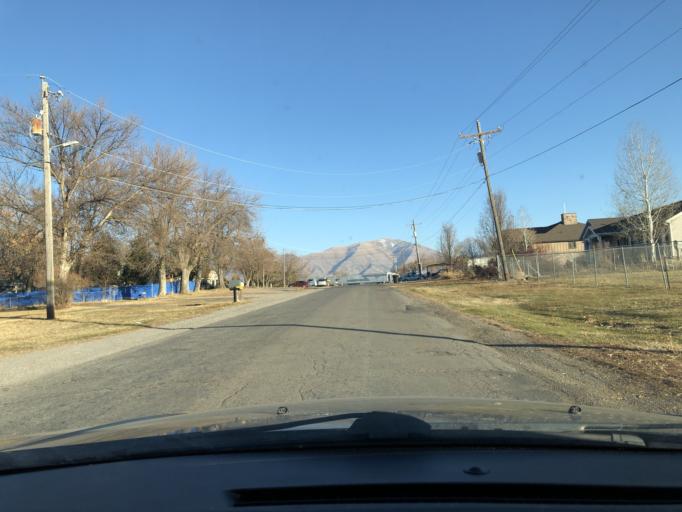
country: US
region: Utah
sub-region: Cache County
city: Wellsville
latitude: 41.6471
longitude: -111.9145
